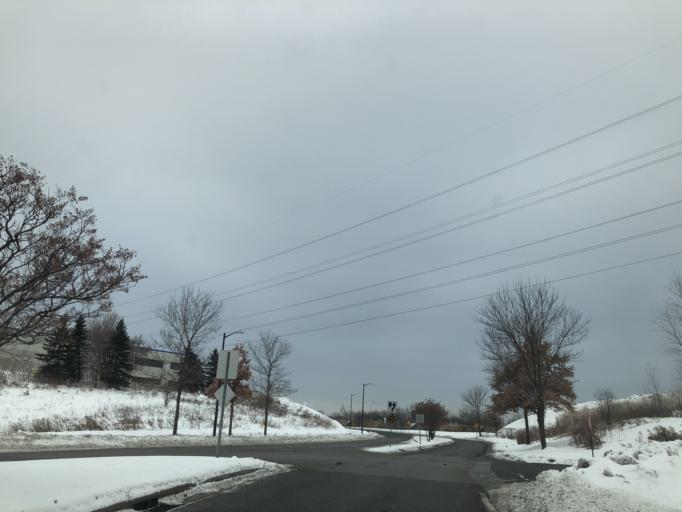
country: US
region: Minnesota
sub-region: Ramsey County
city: New Brighton
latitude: 45.0780
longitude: -93.1827
